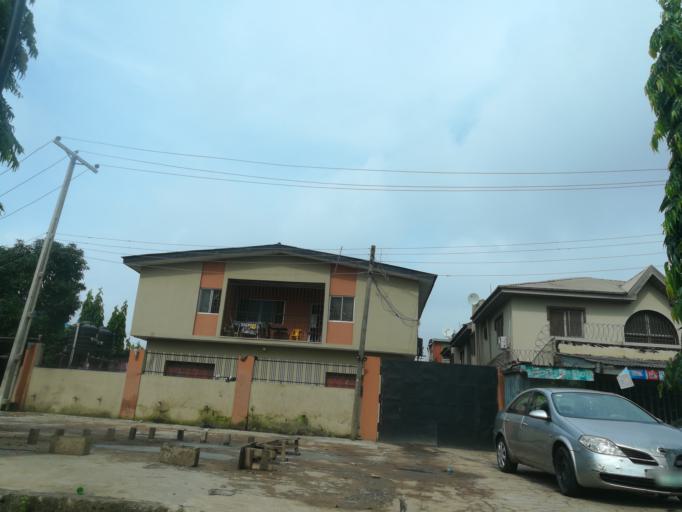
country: NG
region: Lagos
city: Agege
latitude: 6.6010
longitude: 3.3097
